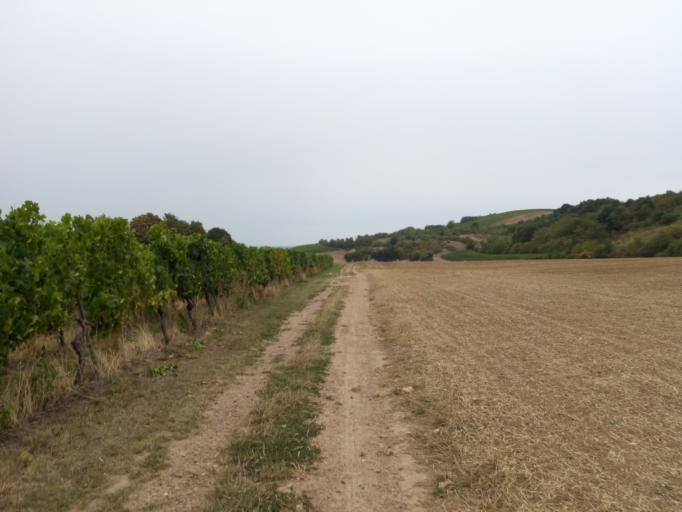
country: DE
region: Rheinland-Pfalz
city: Rummelsheim
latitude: 49.9244
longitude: 7.8554
